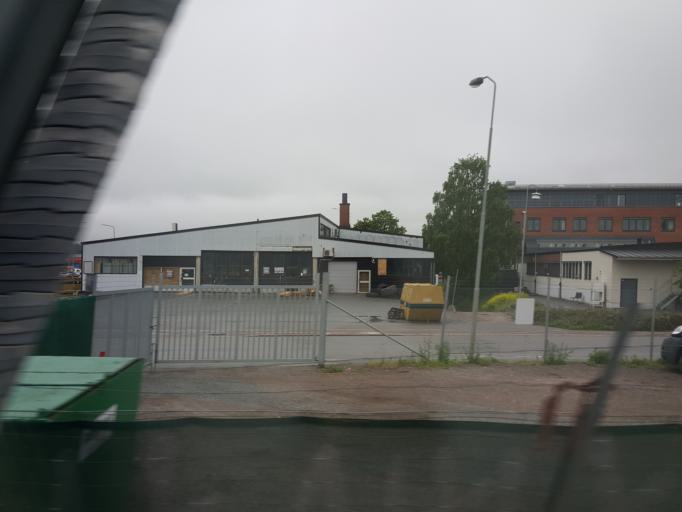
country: SE
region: Uppsala
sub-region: Uppsala Kommun
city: Uppsala
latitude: 59.8488
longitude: 17.6648
